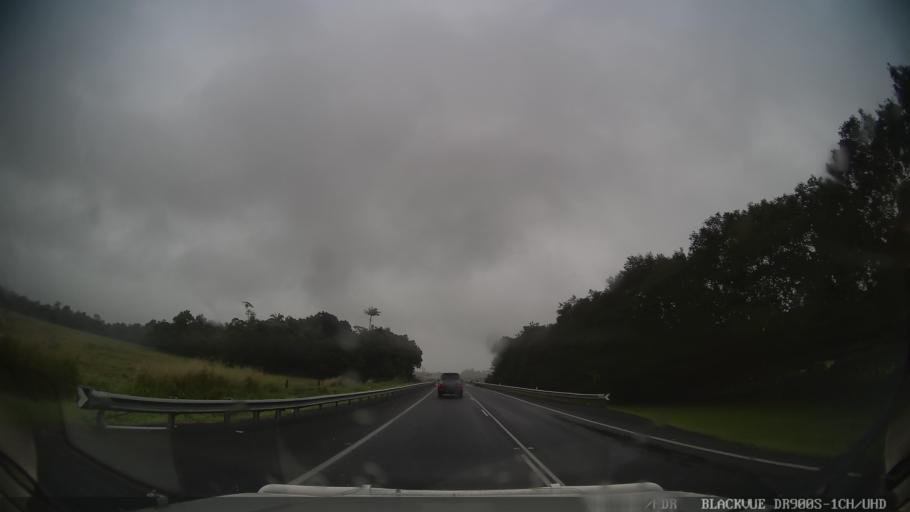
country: AU
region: Queensland
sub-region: Cassowary Coast
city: Innisfail
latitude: -17.6499
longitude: 146.0331
